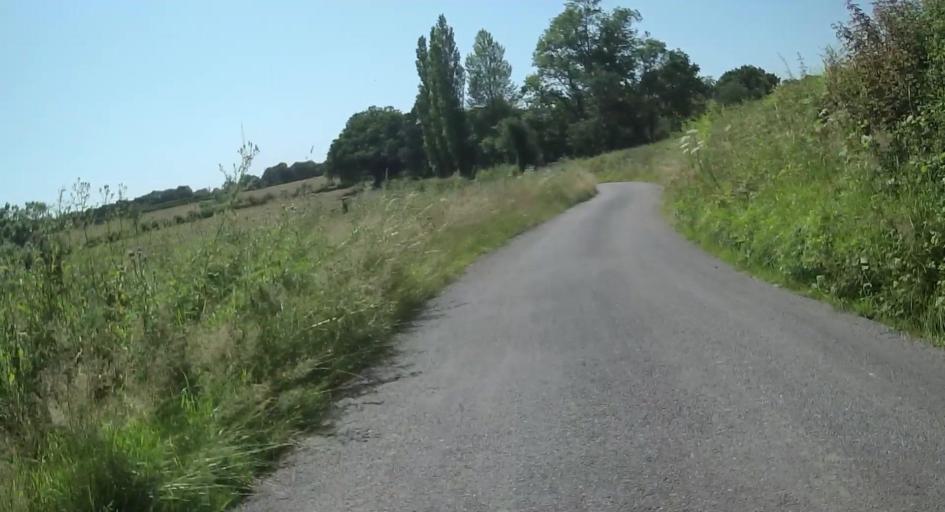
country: GB
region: England
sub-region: Surrey
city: Churt
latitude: 51.1525
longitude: -0.8162
